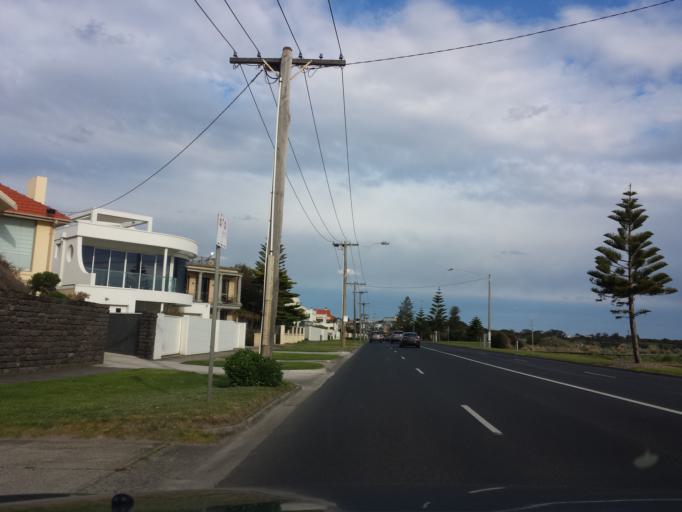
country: AU
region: Victoria
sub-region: Bayside
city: Hampton
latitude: -37.9351
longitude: 144.9961
